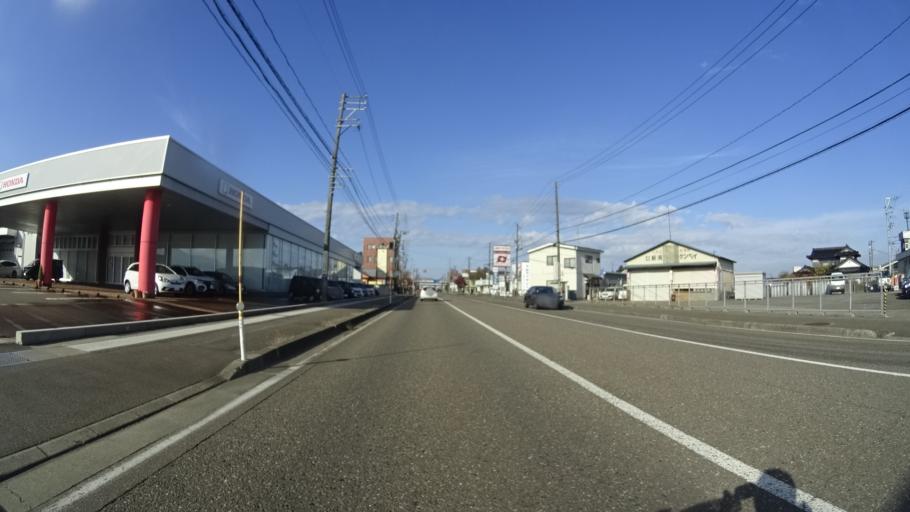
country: JP
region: Niigata
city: Joetsu
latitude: 37.1395
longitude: 138.2408
